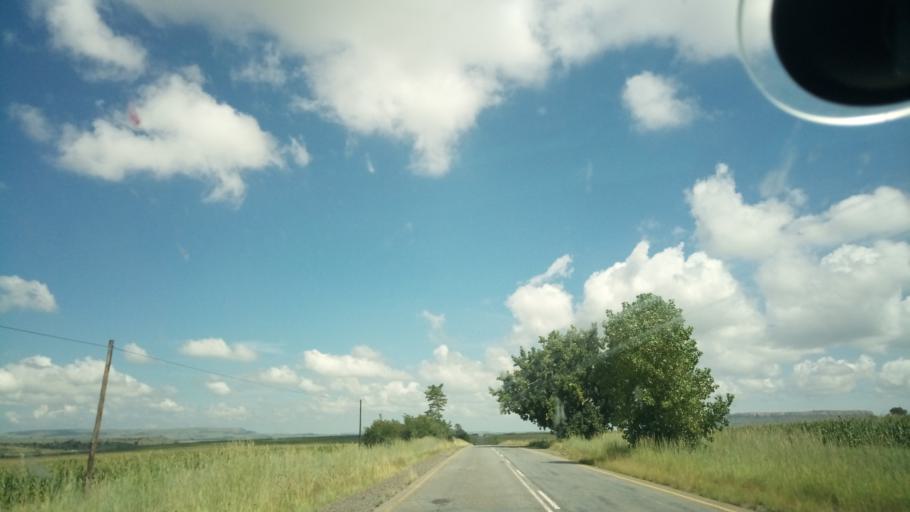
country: ZA
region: Orange Free State
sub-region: Thabo Mofutsanyana District Municipality
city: Ficksburg
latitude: -28.9032
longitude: 27.7969
